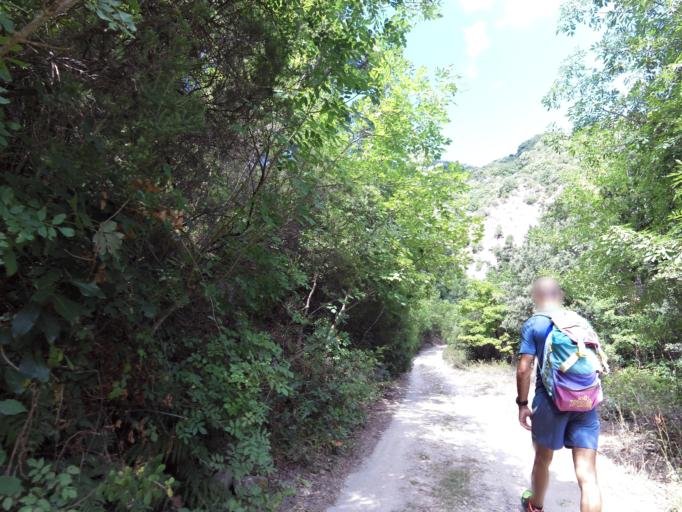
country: IT
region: Calabria
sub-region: Provincia di Reggio Calabria
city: Bivongi
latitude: 38.4911
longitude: 16.4037
